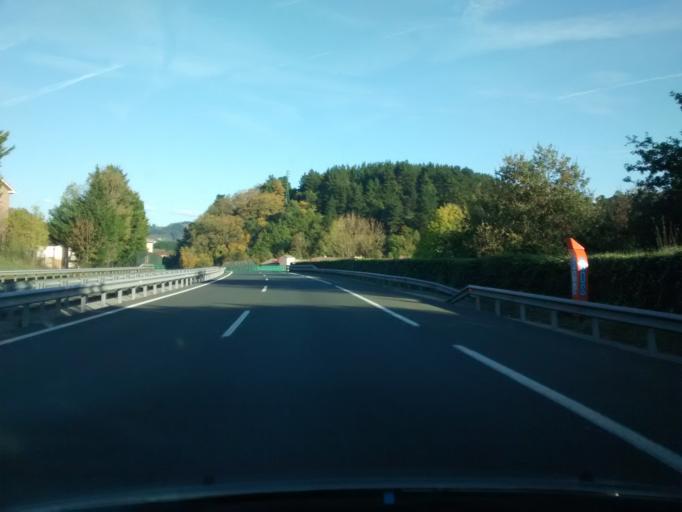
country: ES
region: Basque Country
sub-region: Bizkaia
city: Berriz
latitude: 43.1675
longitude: -2.5769
